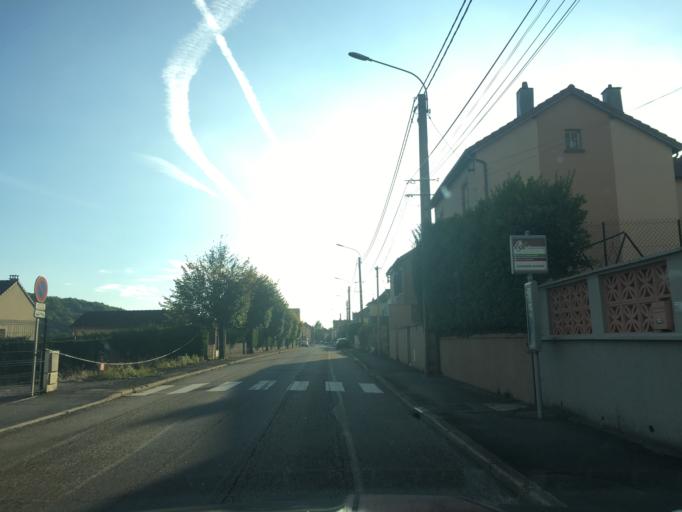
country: FR
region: Lorraine
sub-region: Departement de Meurthe-et-Moselle
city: Longlaville
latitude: 49.5275
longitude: 5.8144
